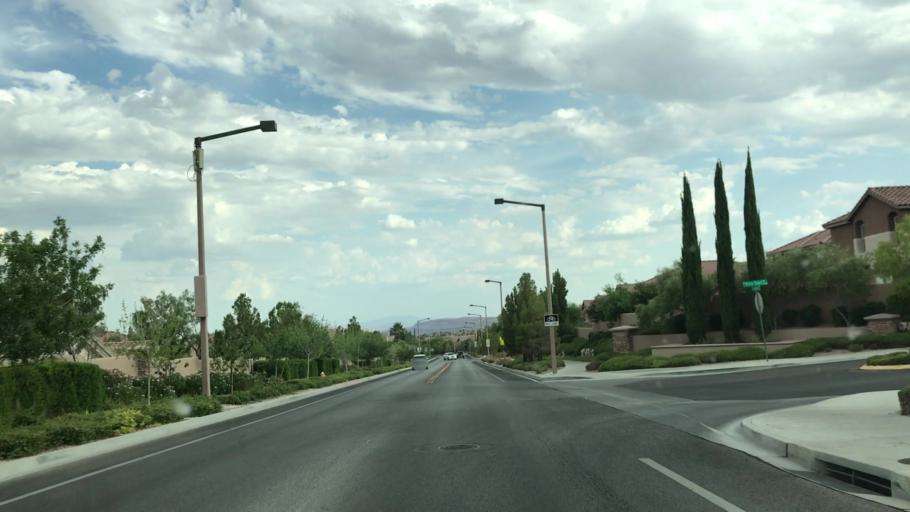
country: US
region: Nevada
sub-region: Clark County
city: Summerlin South
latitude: 36.1667
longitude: -115.3500
